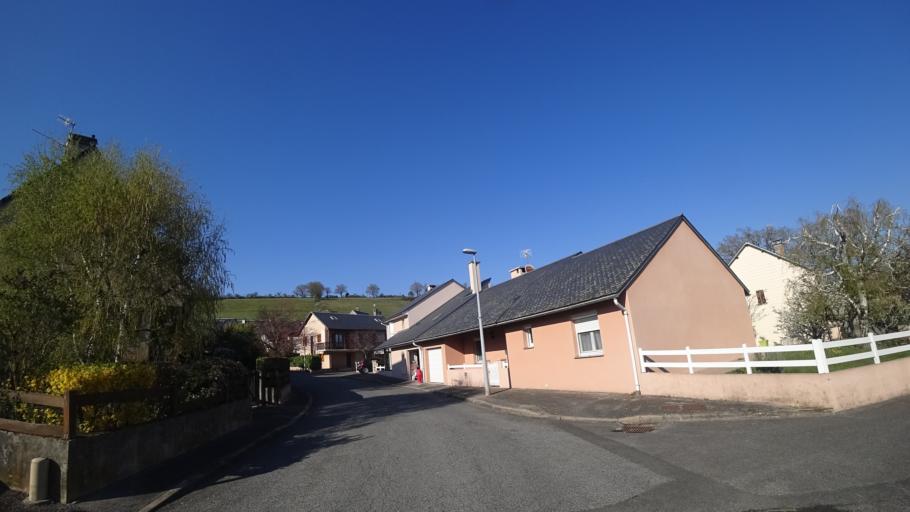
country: FR
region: Midi-Pyrenees
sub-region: Departement de l'Aveyron
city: Sainte-Radegonde
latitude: 44.3629
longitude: 2.6070
